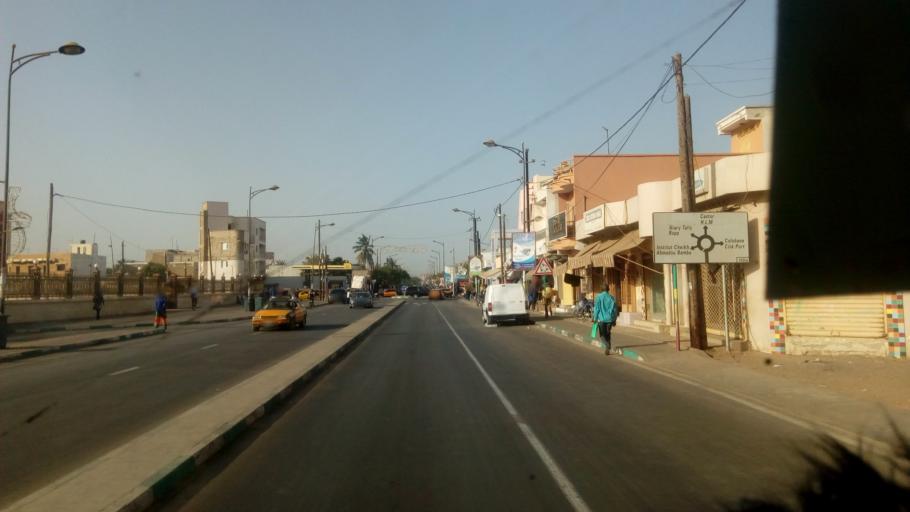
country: SN
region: Dakar
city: Dakar
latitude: 14.7010
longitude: -17.4470
